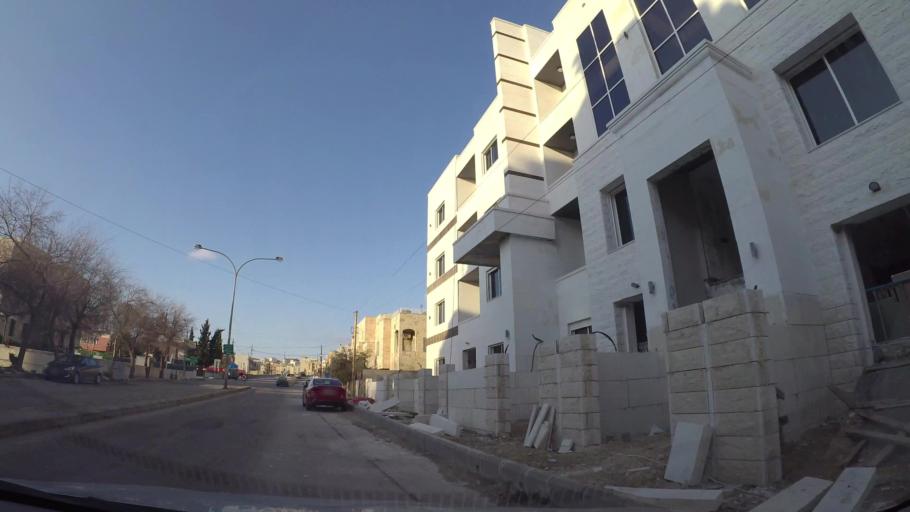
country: JO
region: Amman
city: Al Jubayhah
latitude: 31.9933
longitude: 35.8661
